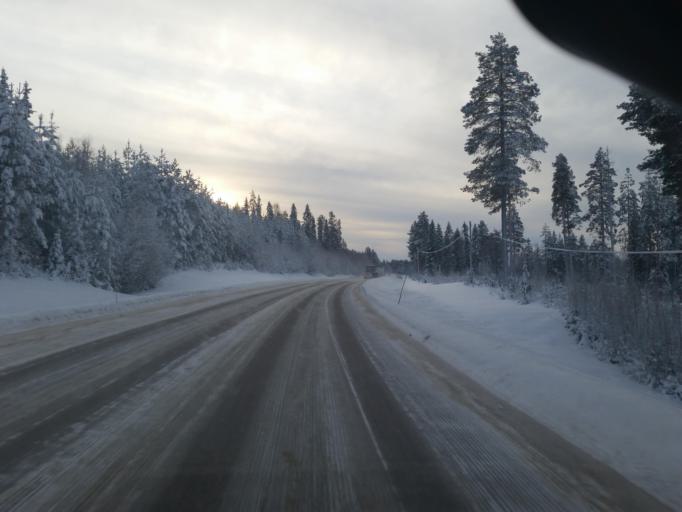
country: SE
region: Norrbotten
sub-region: Alvsbyns Kommun
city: AElvsbyn
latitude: 65.6703
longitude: 21.2181
